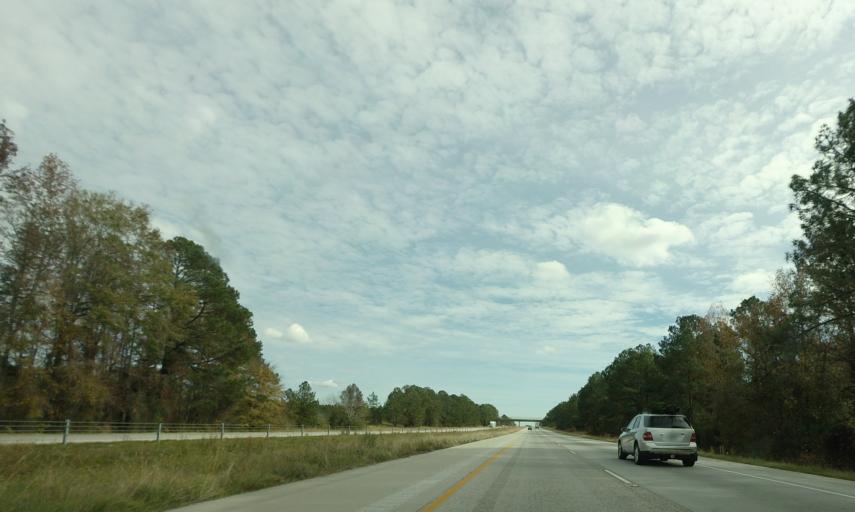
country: US
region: Georgia
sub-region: Laurens County
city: Dublin
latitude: 32.5070
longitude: -83.0352
